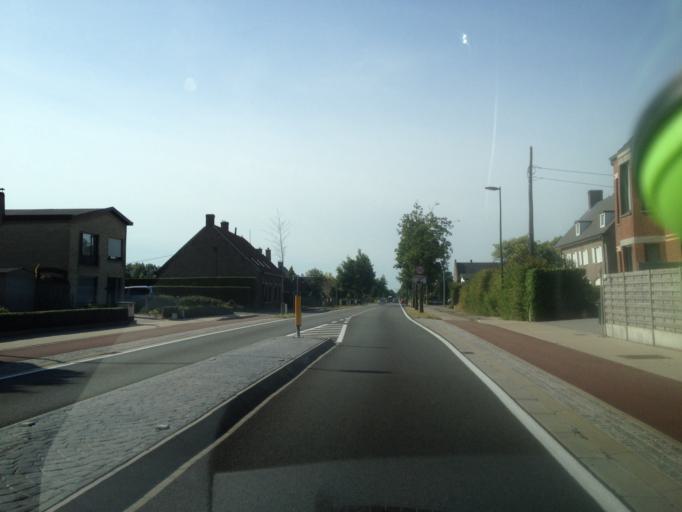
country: BE
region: Flanders
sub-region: Provincie West-Vlaanderen
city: Oudenburg
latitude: 51.1672
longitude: 3.0139
